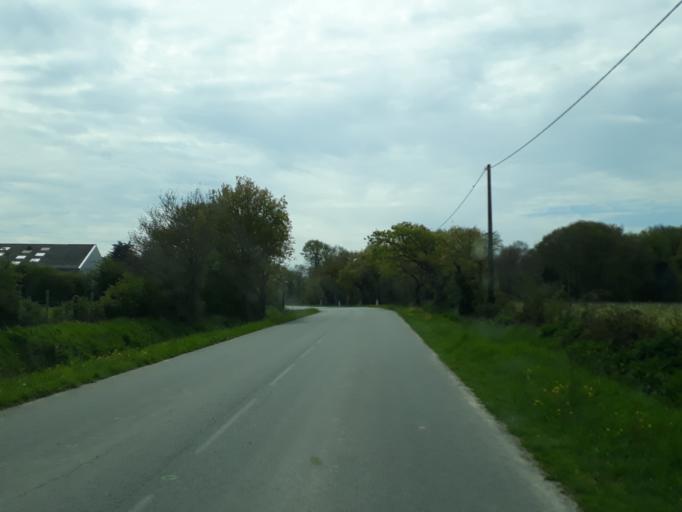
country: FR
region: Pays de la Loire
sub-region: Departement de la Loire-Atlantique
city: Saint-Molf
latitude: 47.3672
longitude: -2.4123
